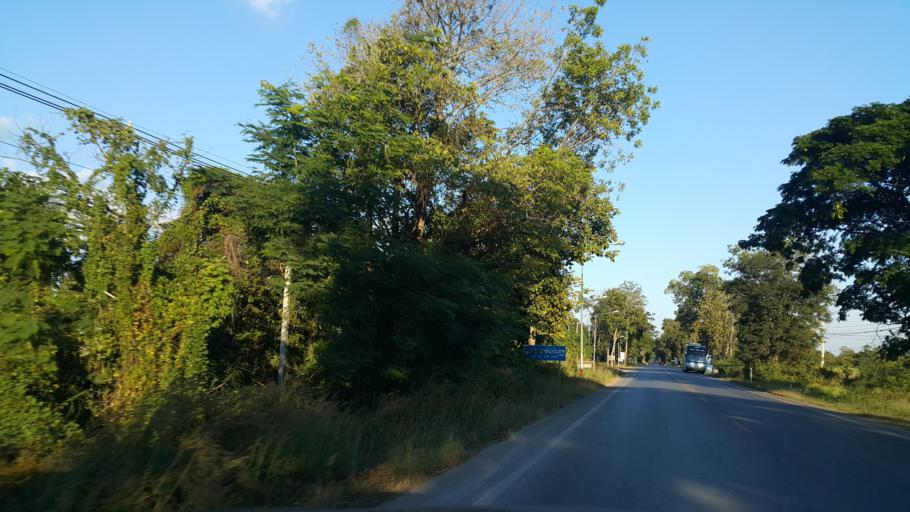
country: TH
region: Sukhothai
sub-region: Amphoe Si Satchanalai
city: Si Satchanalai
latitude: 17.5474
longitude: 99.8475
